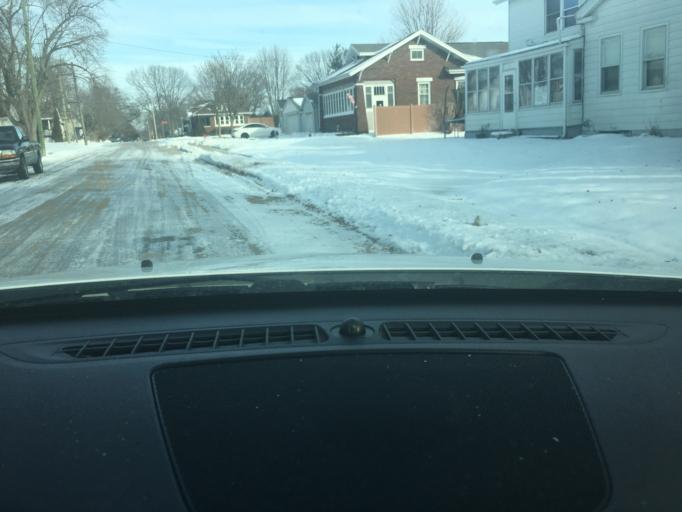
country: US
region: Illinois
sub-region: LaSalle County
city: Peru
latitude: 41.3305
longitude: -89.1278
